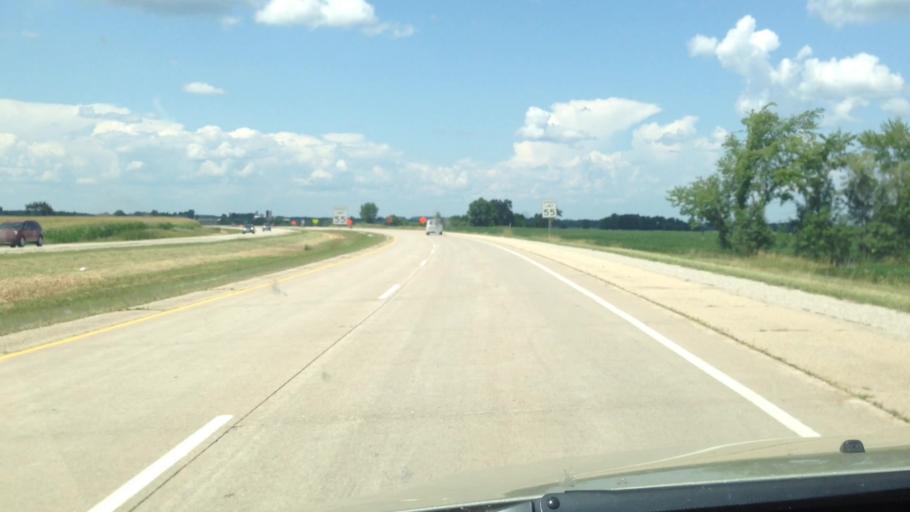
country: US
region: Wisconsin
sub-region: Brown County
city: Pulaski
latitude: 44.6813
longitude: -88.3117
